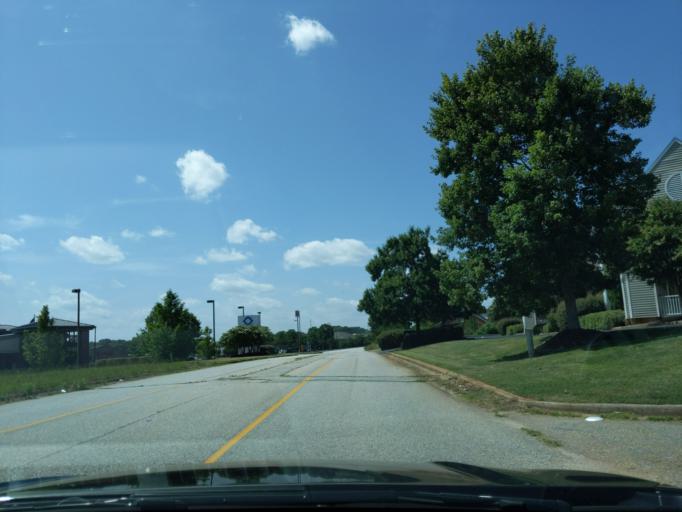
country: US
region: South Carolina
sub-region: Spartanburg County
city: Saxon
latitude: 34.9852
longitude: -81.9692
